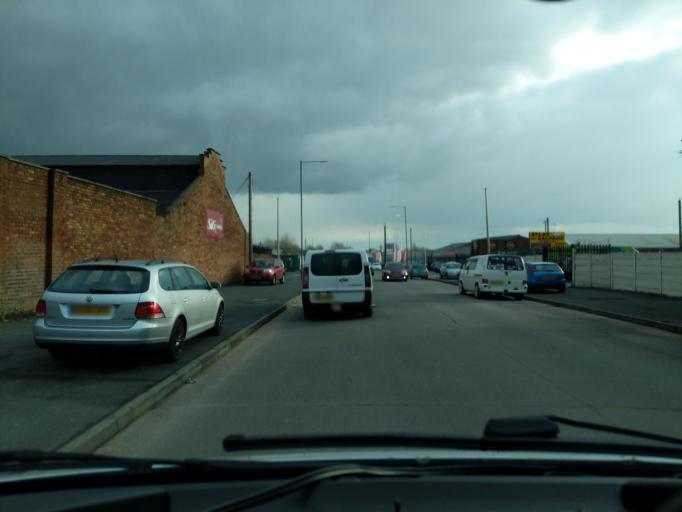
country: GB
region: England
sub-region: St. Helens
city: St Helens
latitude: 53.4519
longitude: -2.7229
